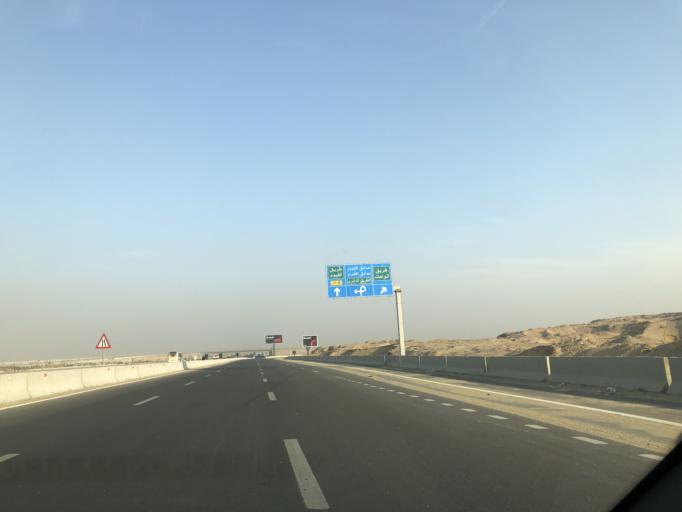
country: EG
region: Al Jizah
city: Madinat Sittah Uktubar
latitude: 29.8970
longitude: 30.9961
